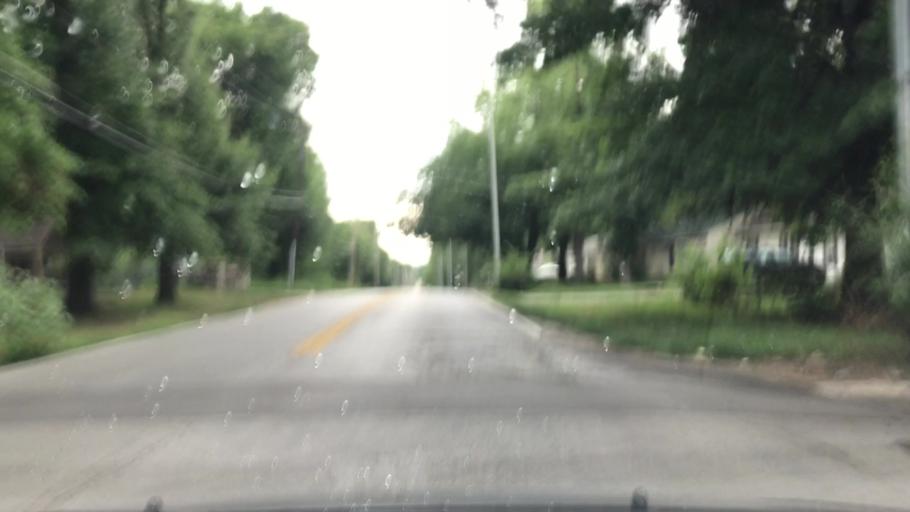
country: US
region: Missouri
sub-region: Jackson County
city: Grandview
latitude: 38.9302
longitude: -94.4996
